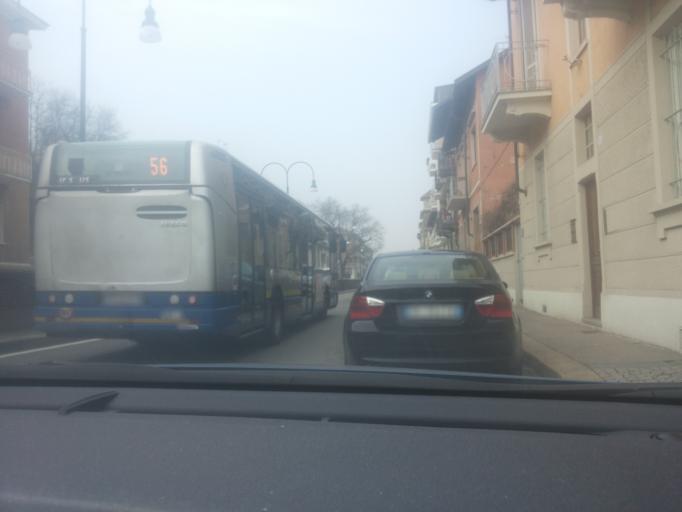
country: IT
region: Piedmont
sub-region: Provincia di Torino
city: Turin
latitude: 45.0658
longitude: 7.7161
